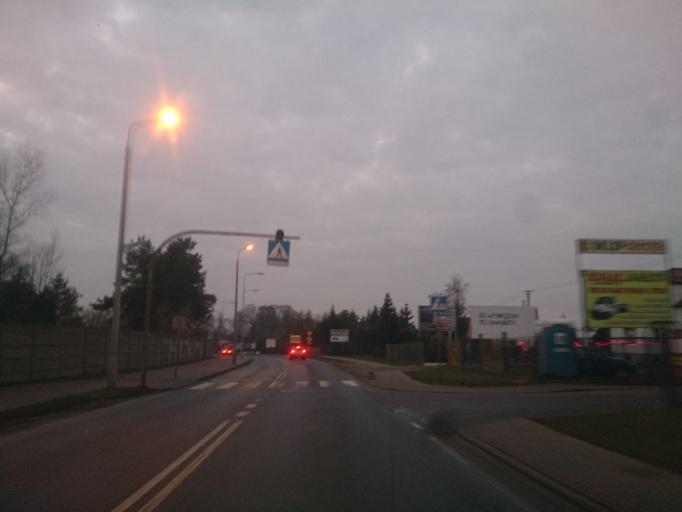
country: PL
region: Kujawsko-Pomorskie
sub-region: Grudziadz
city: Grudziadz
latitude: 53.4564
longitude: 18.7866
